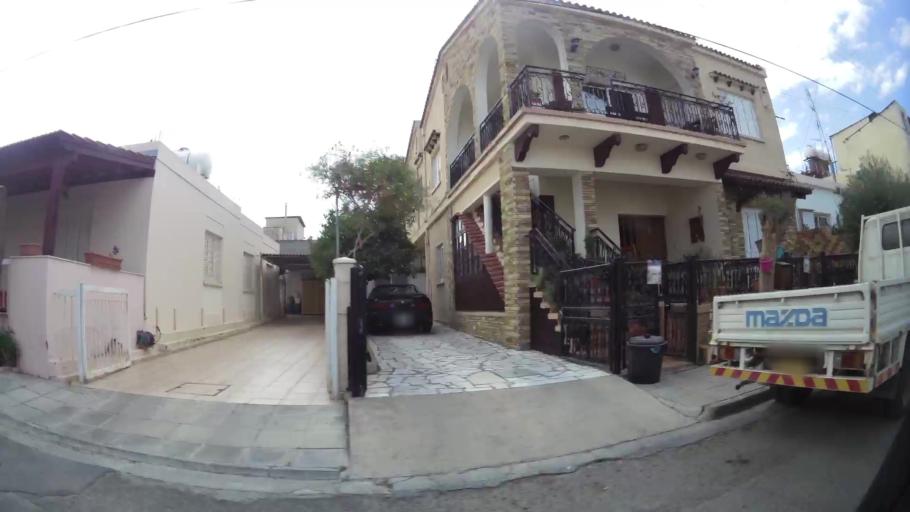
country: CY
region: Lefkosia
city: Nicosia
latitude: 35.1789
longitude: 33.3880
